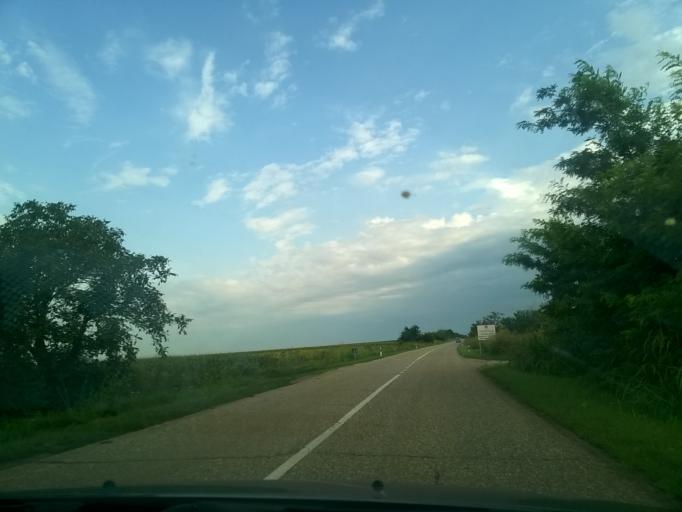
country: RS
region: Autonomna Pokrajina Vojvodina
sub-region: Juznobanatski Okrug
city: Kovacica
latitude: 45.1279
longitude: 20.6160
